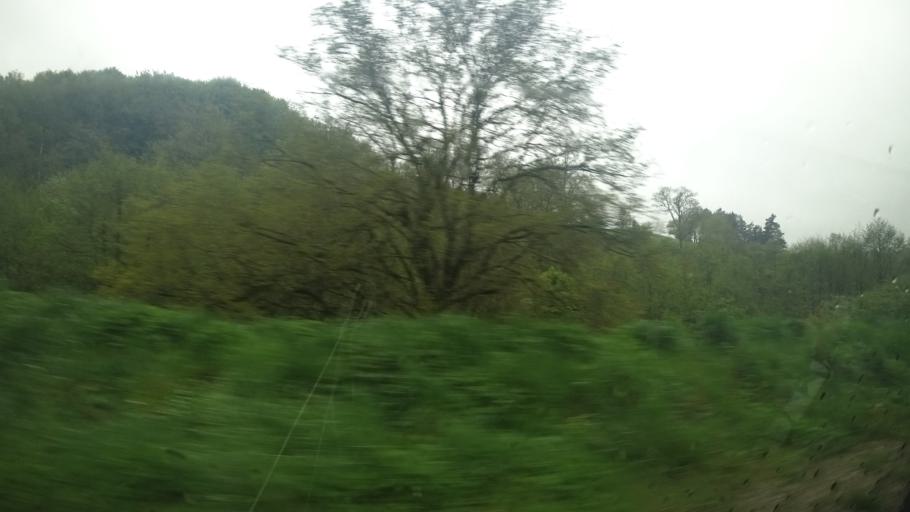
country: FR
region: Midi-Pyrenees
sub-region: Departement de l'Aveyron
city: Laissac
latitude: 44.2669
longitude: 2.8976
